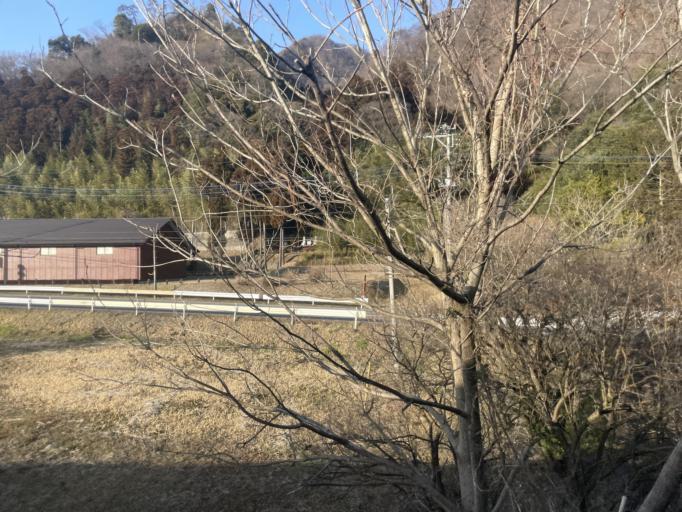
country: JP
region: Gunma
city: Nakanojomachi
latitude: 36.5655
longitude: 138.8934
